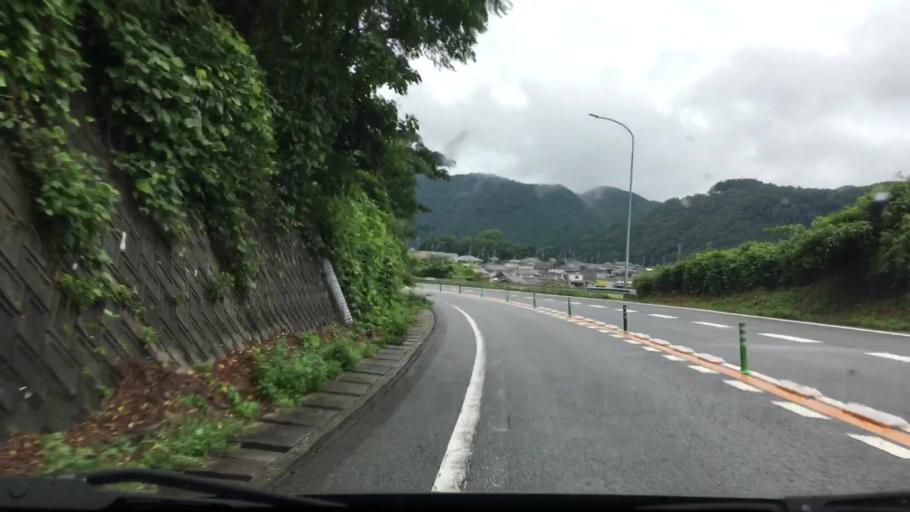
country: JP
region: Hyogo
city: Himeji
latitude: 35.0148
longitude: 134.7612
